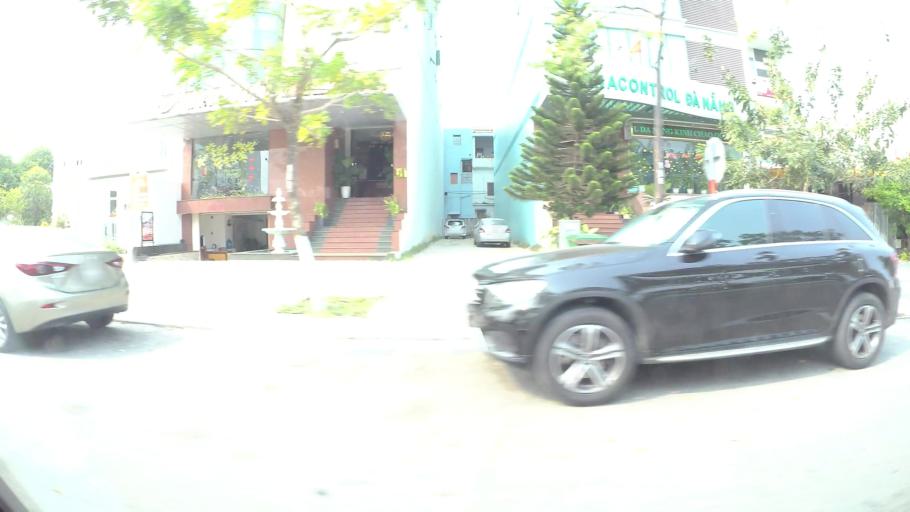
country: VN
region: Da Nang
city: Cam Le
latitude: 16.0398
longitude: 108.2122
